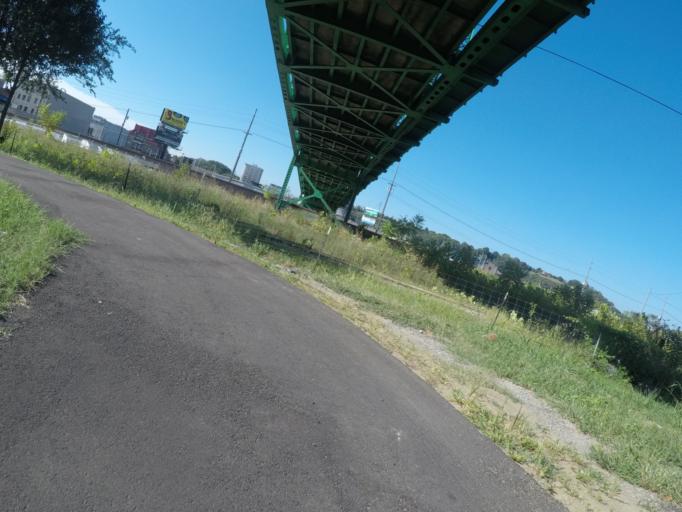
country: US
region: Kentucky
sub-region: Boyd County
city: Ashland
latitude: 38.4831
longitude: -82.6423
